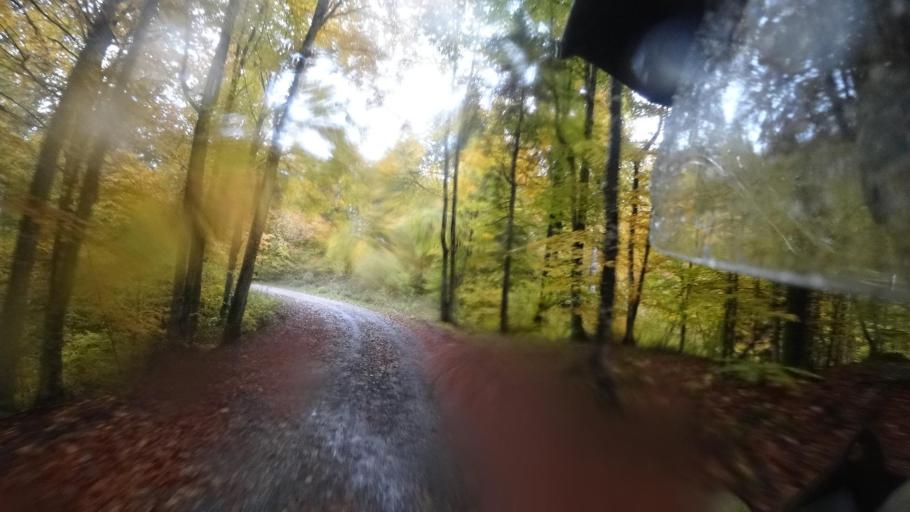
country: HR
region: Primorsko-Goranska
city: Vrbovsko
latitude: 45.3574
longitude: 15.0729
